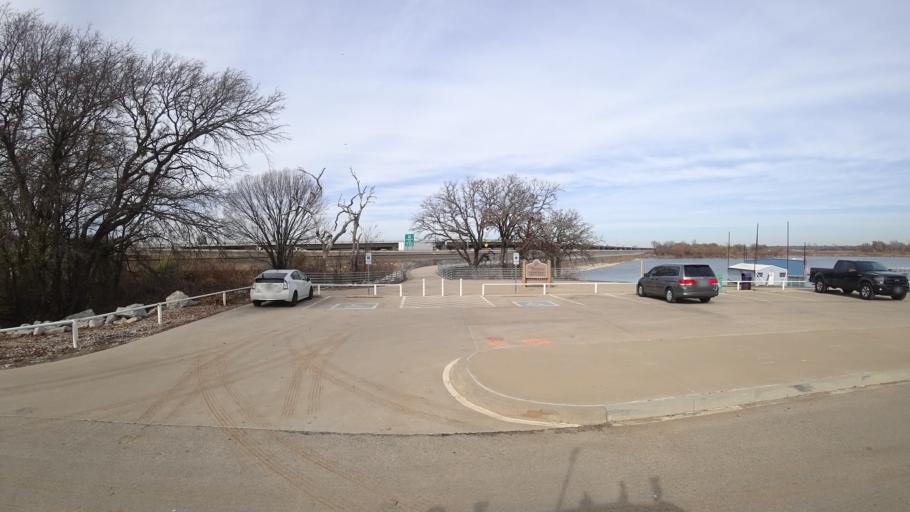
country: US
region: Texas
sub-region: Denton County
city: Highland Village
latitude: 33.0871
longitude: -97.0261
